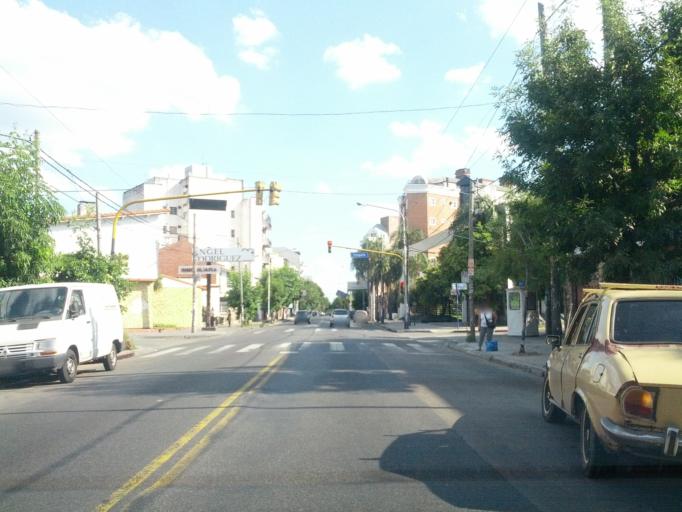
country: AR
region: Buenos Aires
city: San Justo
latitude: -34.6510
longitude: -58.5636
